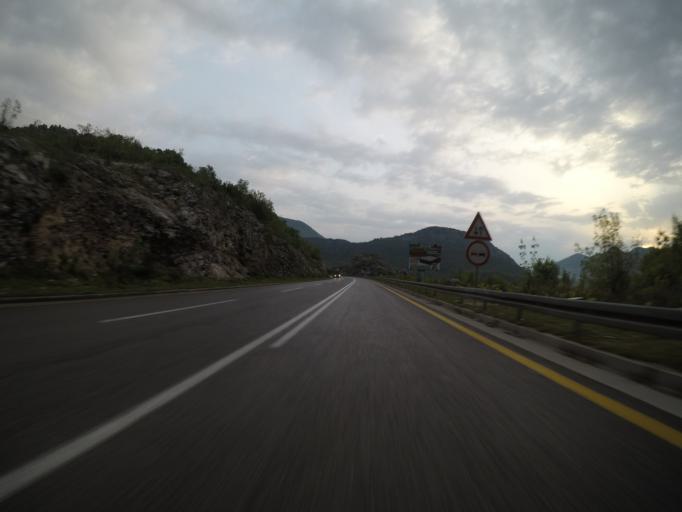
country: ME
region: Bar
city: Sutomore
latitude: 42.2177
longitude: 19.0508
